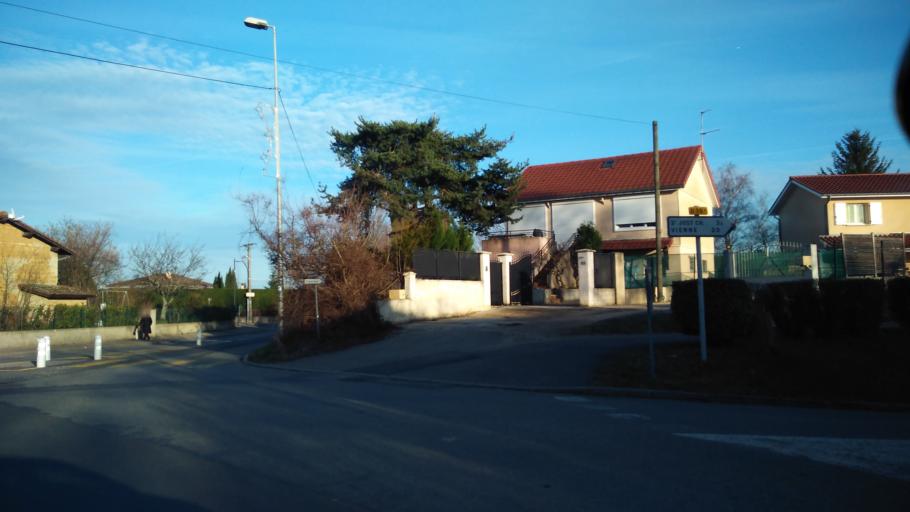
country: FR
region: Rhone-Alpes
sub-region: Departement de l'Isere
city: Valencin
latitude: 45.6136
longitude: 5.0183
